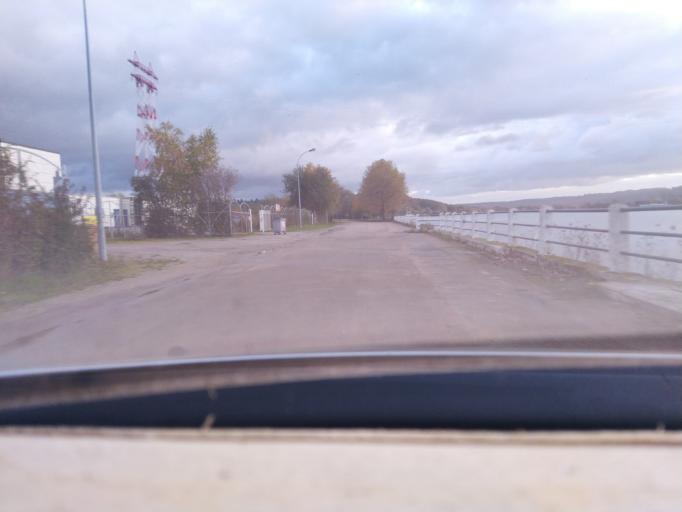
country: FR
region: Haute-Normandie
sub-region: Departement de la Seine-Maritime
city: Le Trait
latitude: 49.4610
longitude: 0.8182
